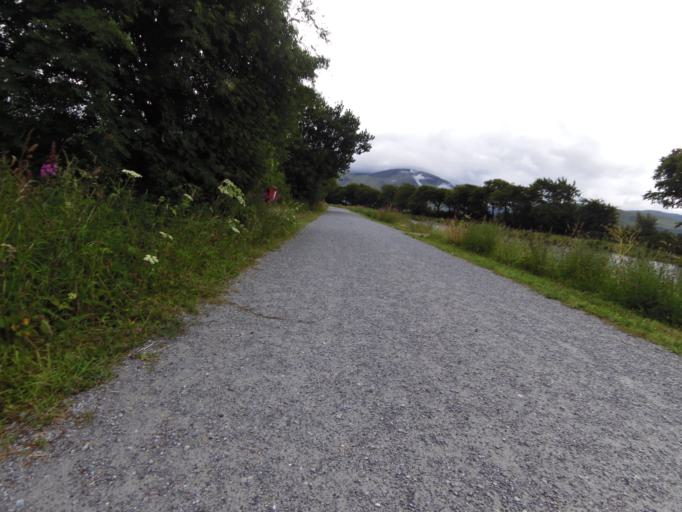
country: GB
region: Scotland
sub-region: Highland
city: Fort William
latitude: 56.8414
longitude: -5.1127
